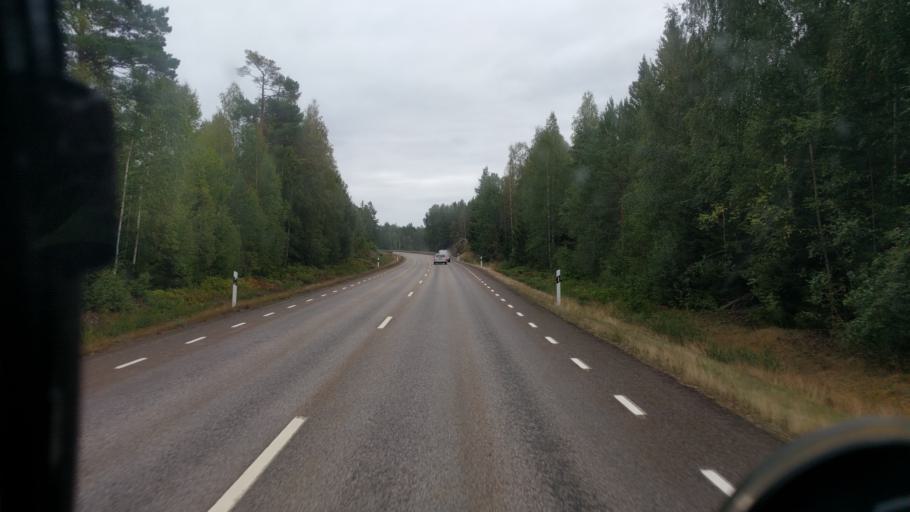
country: SE
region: Kalmar
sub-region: Vasterviks Kommun
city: Ankarsrum
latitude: 57.7022
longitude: 16.2191
